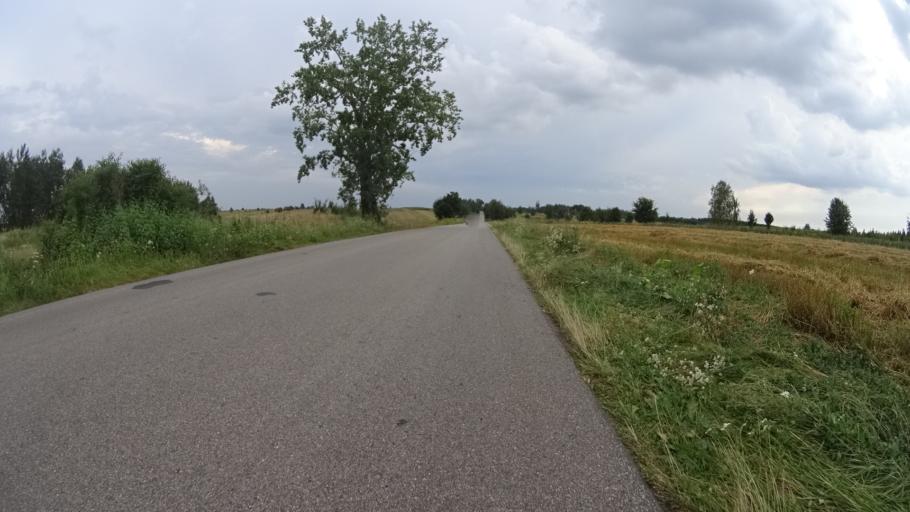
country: PL
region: Masovian Voivodeship
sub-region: Powiat grojecki
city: Goszczyn
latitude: 51.6748
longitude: 20.8584
